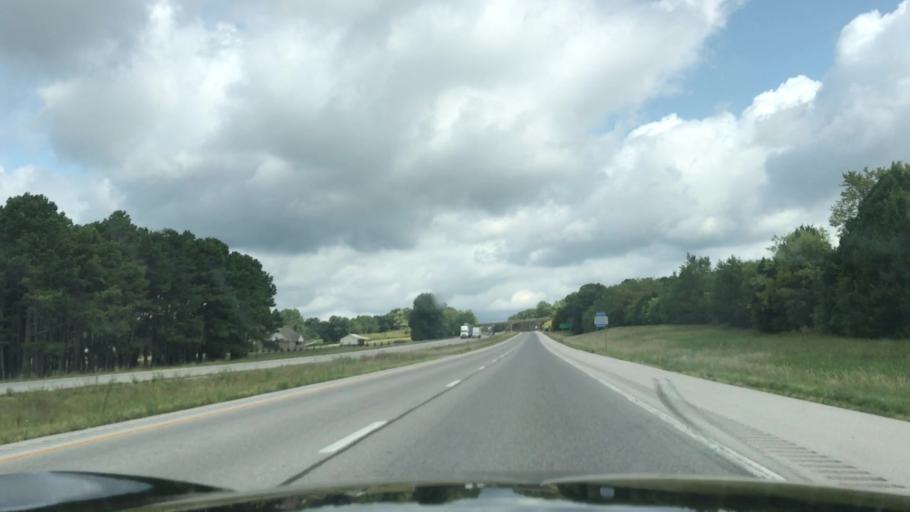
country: US
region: Kentucky
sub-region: Warren County
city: Bowling Green
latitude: 36.9970
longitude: -86.5052
